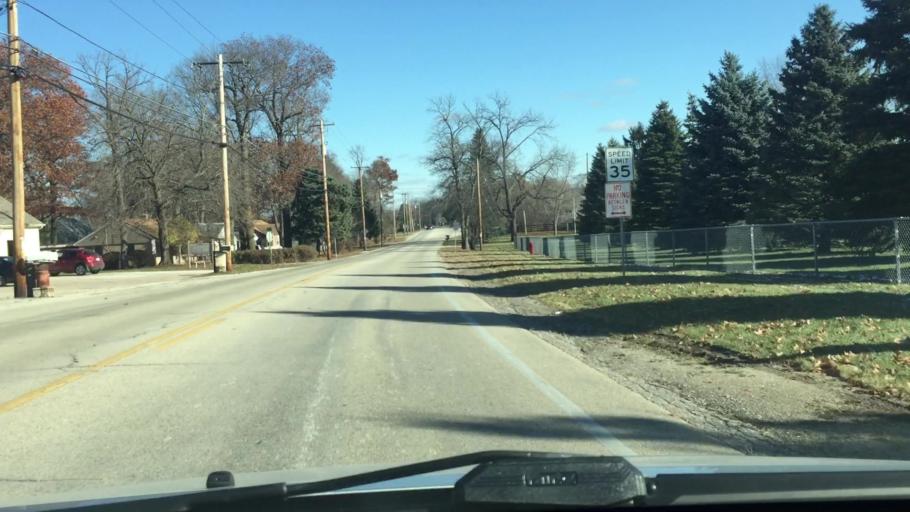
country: US
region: Wisconsin
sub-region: Waukesha County
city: Pewaukee
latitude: 43.0669
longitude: -88.2946
